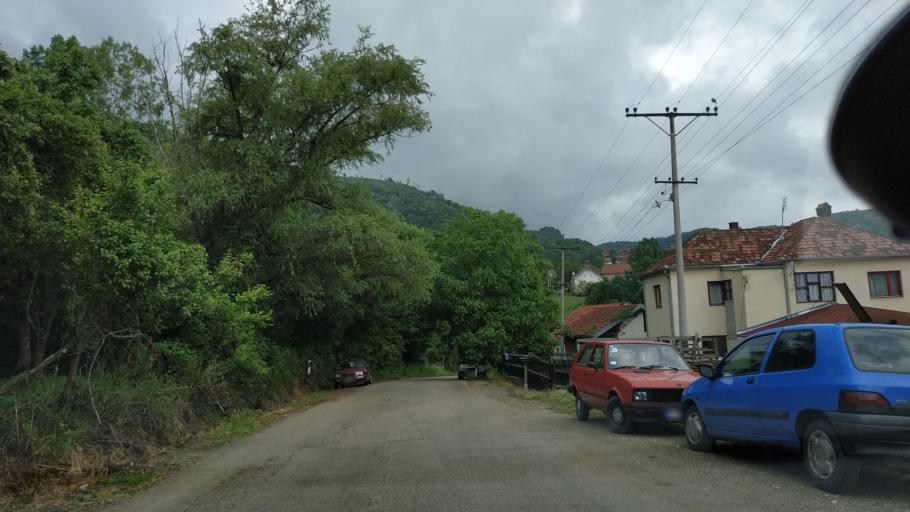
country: RS
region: Central Serbia
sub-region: Toplicki Okrug
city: Prokuplje
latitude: 43.3980
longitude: 21.5543
